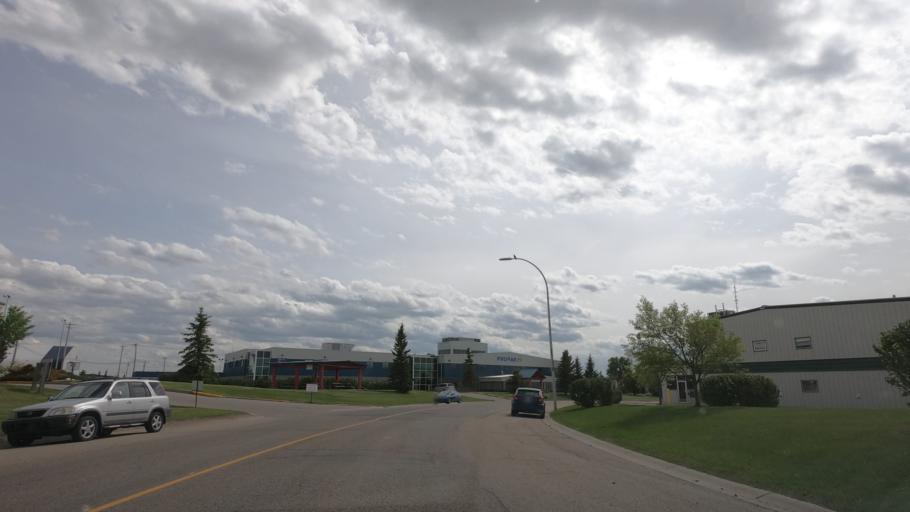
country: CA
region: Alberta
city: Airdrie
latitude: 51.2894
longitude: -113.9808
